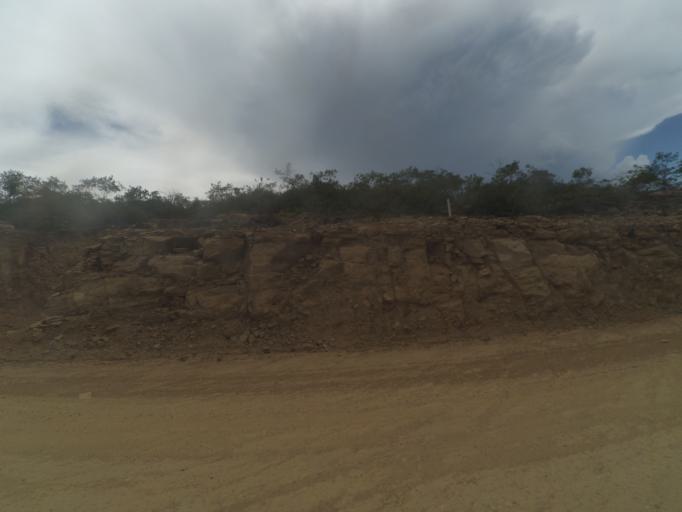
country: BO
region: Chuquisaca
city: Padilla
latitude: -19.3490
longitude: -64.2891
